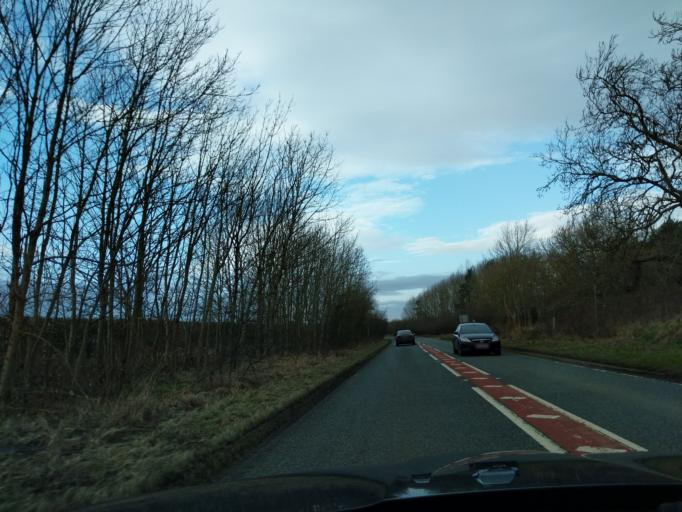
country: GB
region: England
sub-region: Northumberland
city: Darras Hall
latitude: 55.0763
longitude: -1.7991
